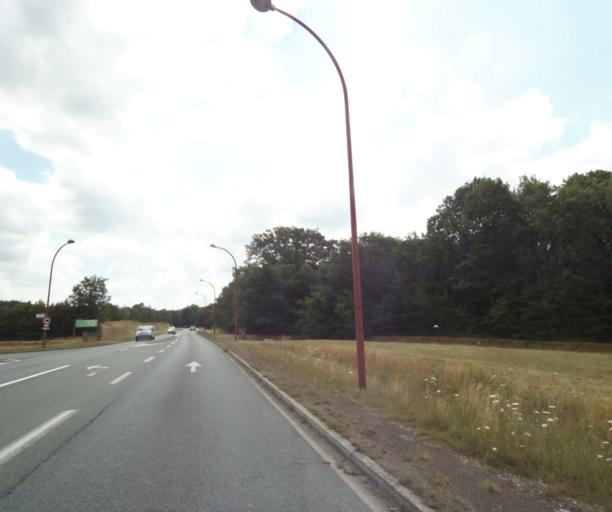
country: FR
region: Centre
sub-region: Departement du Loiret
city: Saint-Cyr-en-Val
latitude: 47.8134
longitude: 1.9297
